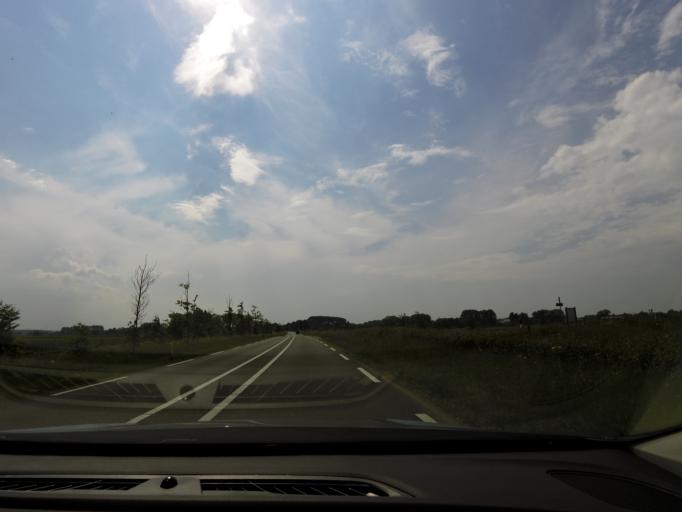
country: NL
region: North Brabant
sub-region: Gemeente Woudrichem
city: Woudrichem
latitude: 51.7929
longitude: 5.0460
